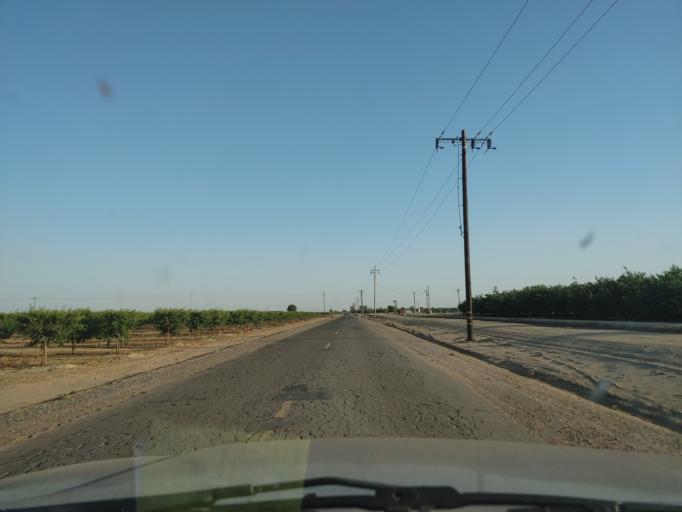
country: US
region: California
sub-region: Madera County
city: Chowchilla
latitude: 37.1291
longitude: -120.3828
